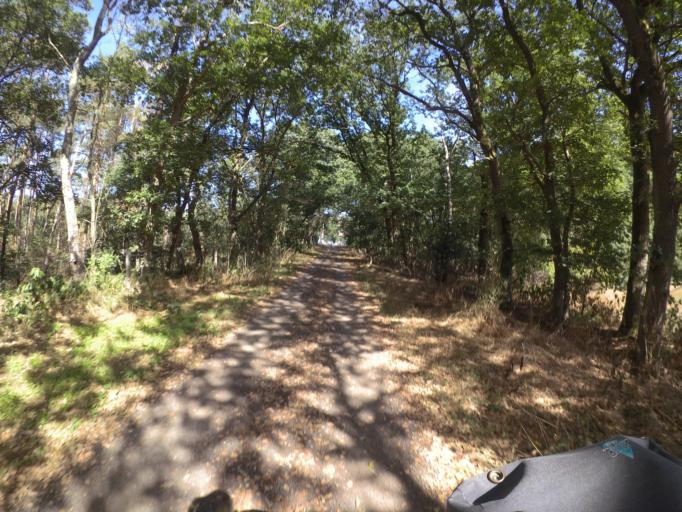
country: NL
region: Overijssel
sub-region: Gemeente Twenterand
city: Den Ham
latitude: 52.3692
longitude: 6.4078
